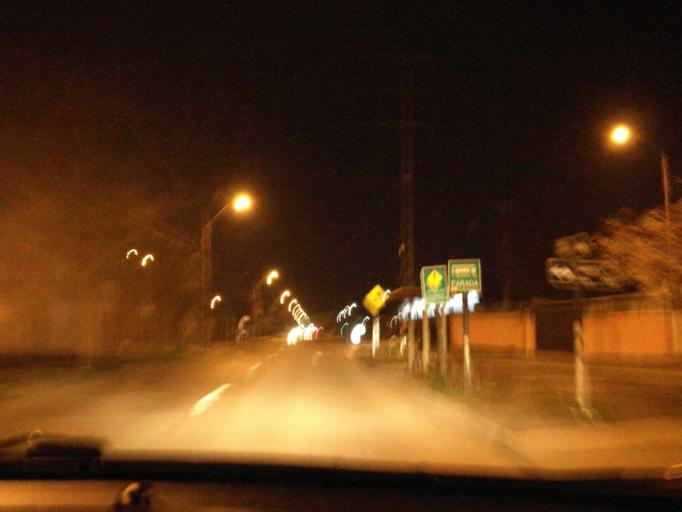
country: CL
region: O'Higgins
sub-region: Provincia de Cachapoal
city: Rancagua
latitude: -34.1822
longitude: -70.7433
